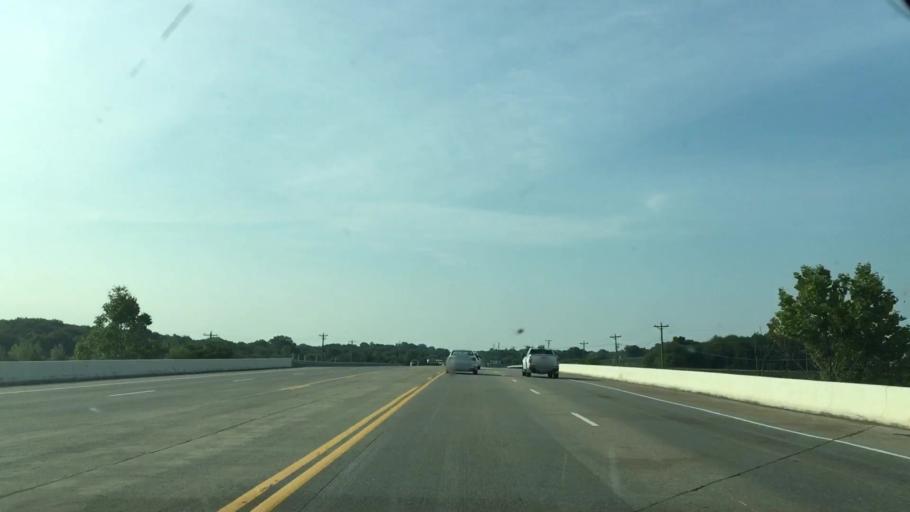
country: US
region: Tennessee
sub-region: Wilson County
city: Mount Juliet
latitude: 36.2268
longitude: -86.4267
